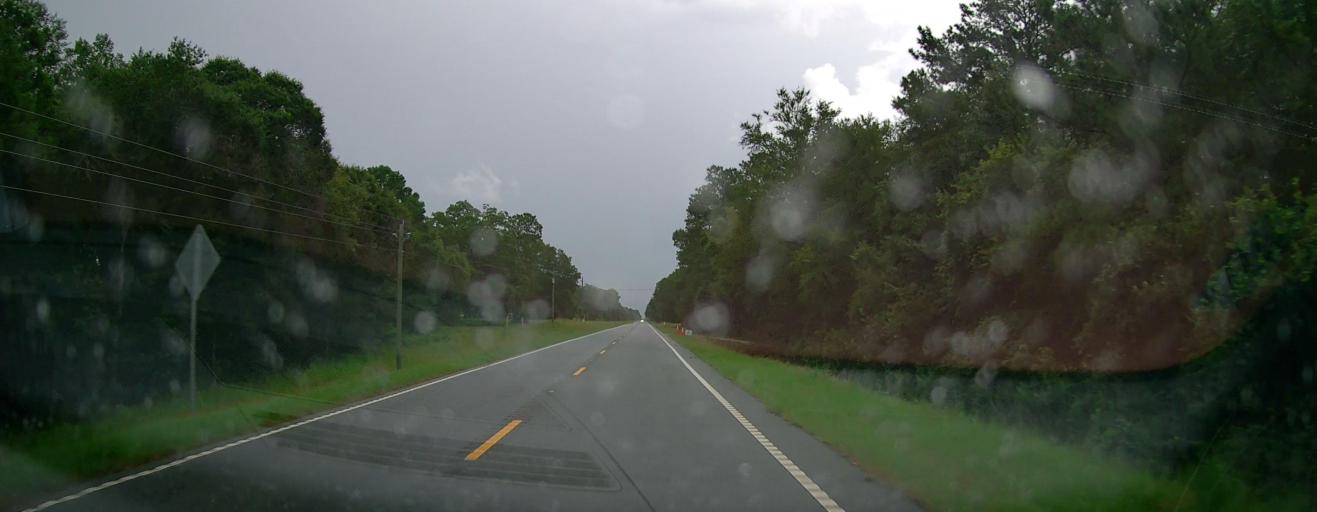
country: US
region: Georgia
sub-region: Brantley County
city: Nahunta
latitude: 31.3434
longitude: -81.9940
